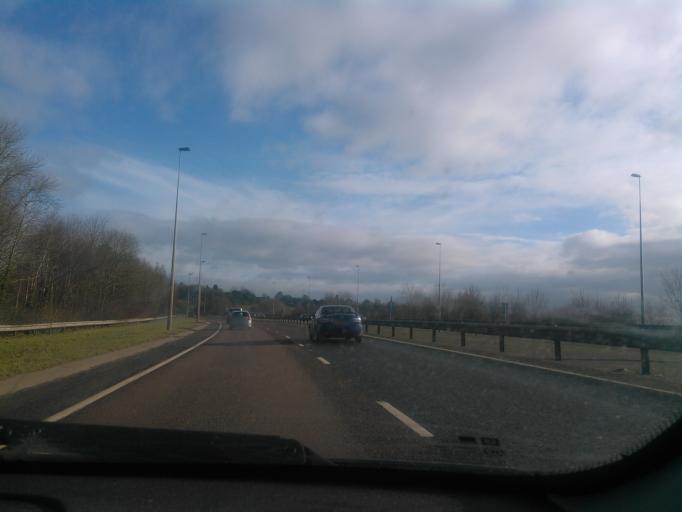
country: GB
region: England
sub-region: Staffordshire
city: Uttoxeter
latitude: 52.9071
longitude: -1.8488
